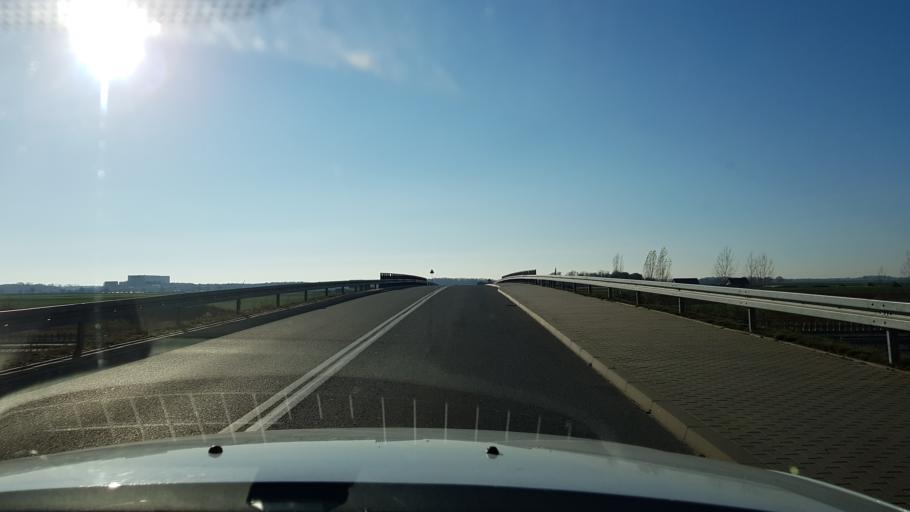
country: PL
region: West Pomeranian Voivodeship
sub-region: Powiat pyrzycki
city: Warnice
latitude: 53.3153
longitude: 14.9826
